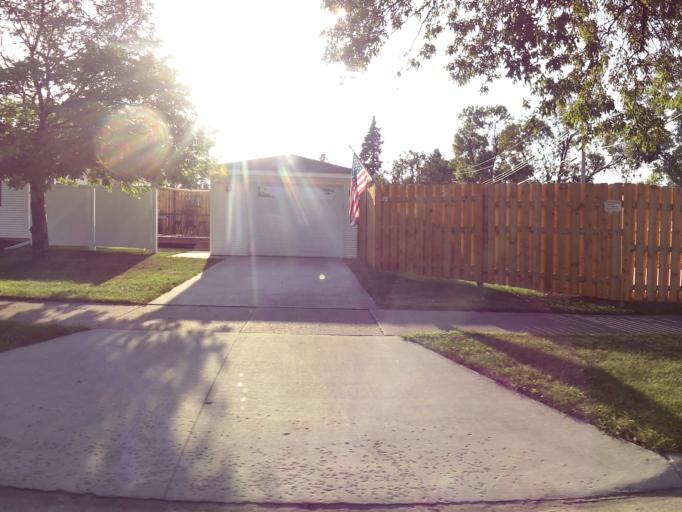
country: US
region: North Dakota
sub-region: Grand Forks County
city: Grand Forks
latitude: 47.8971
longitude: -97.0406
